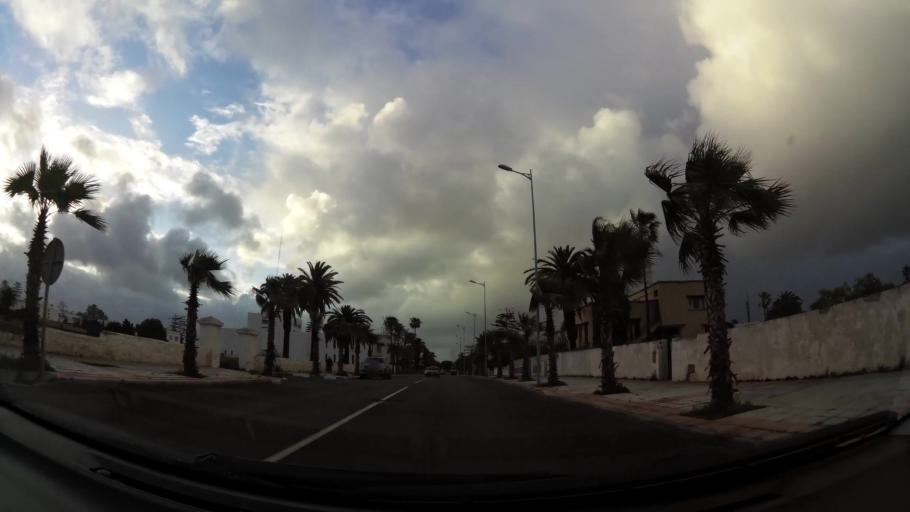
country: MA
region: Doukkala-Abda
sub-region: El-Jadida
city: El Jadida
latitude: 33.2436
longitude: -8.5048
